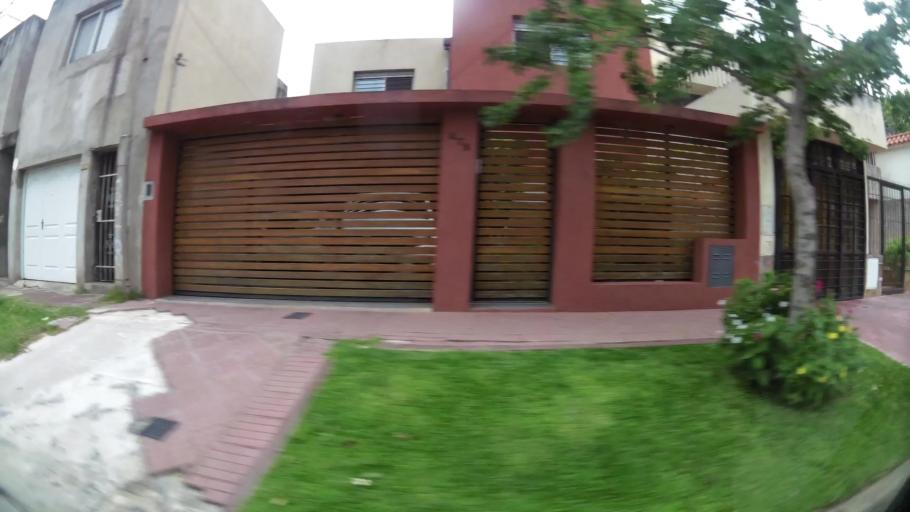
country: AR
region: Santa Fe
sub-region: Departamento de Rosario
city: Rosario
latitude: -32.9102
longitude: -60.6869
